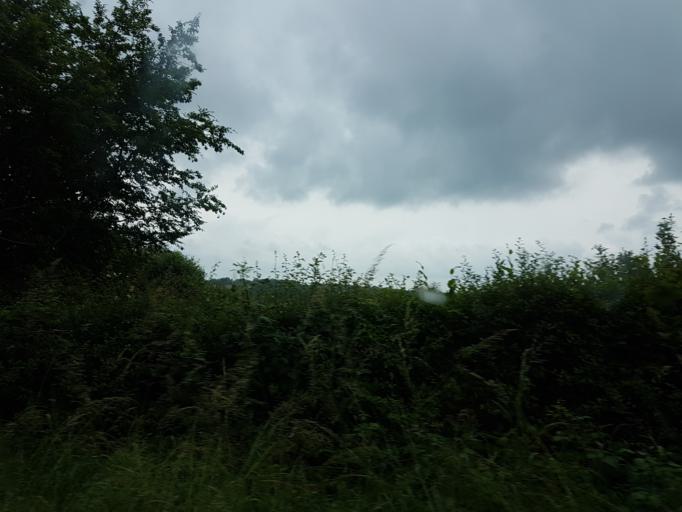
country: FR
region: Bourgogne
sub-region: Departement de la Nievre
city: Corbigny
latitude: 47.1981
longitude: 3.7247
